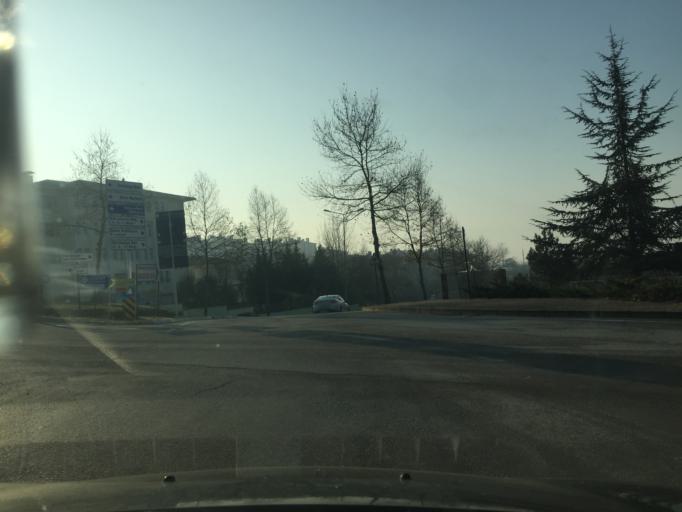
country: TR
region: Duzce
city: Duzce
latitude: 40.8670
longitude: 31.2307
